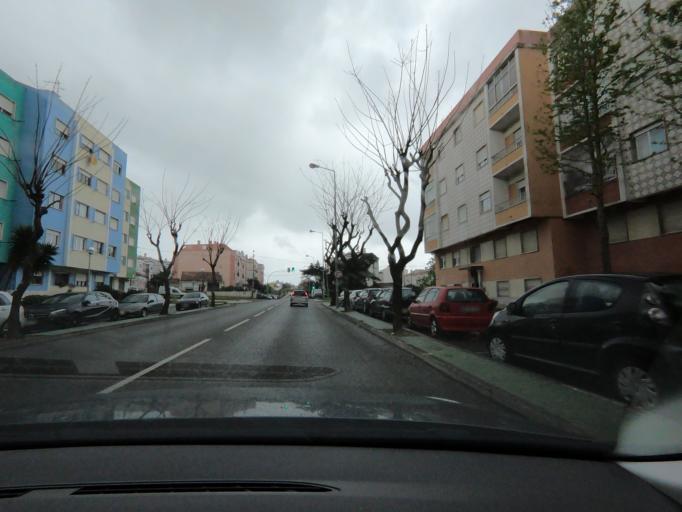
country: PT
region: Lisbon
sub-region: Sintra
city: Rio de Mouro
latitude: 38.7936
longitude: -9.3381
